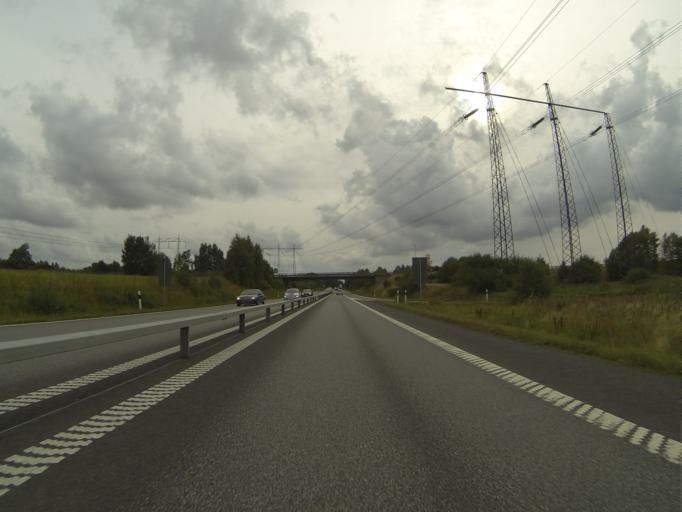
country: SE
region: Skane
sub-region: Horby Kommun
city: Hoerby
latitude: 55.8603
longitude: 13.6423
